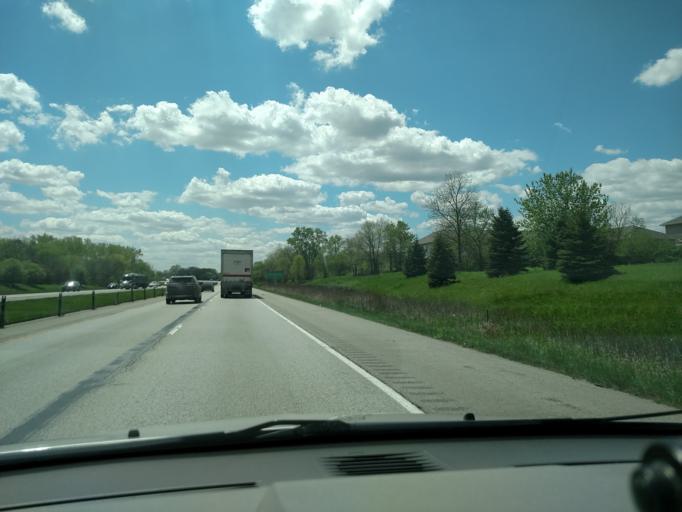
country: US
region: Iowa
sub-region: Polk County
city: Ankeny
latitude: 41.7452
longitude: -93.5763
